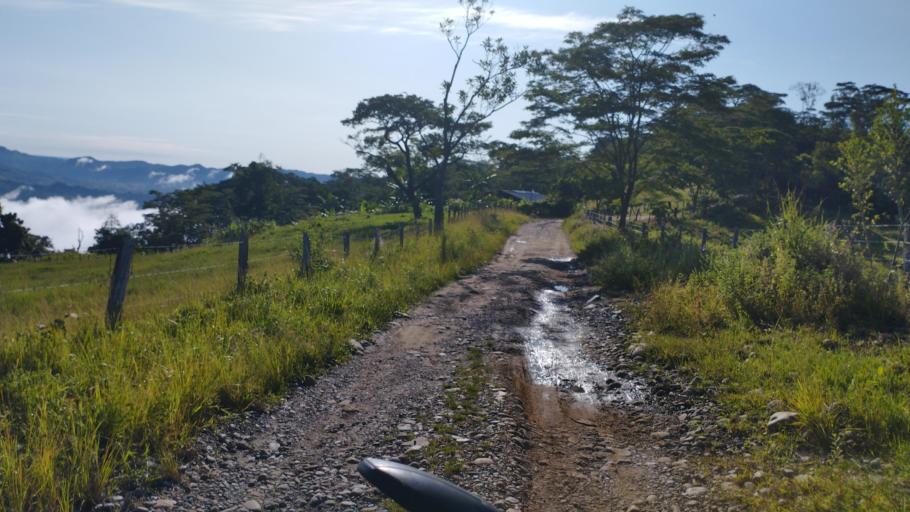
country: CO
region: Boyaca
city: San Luis de Gaceno
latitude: 4.7878
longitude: -73.0919
